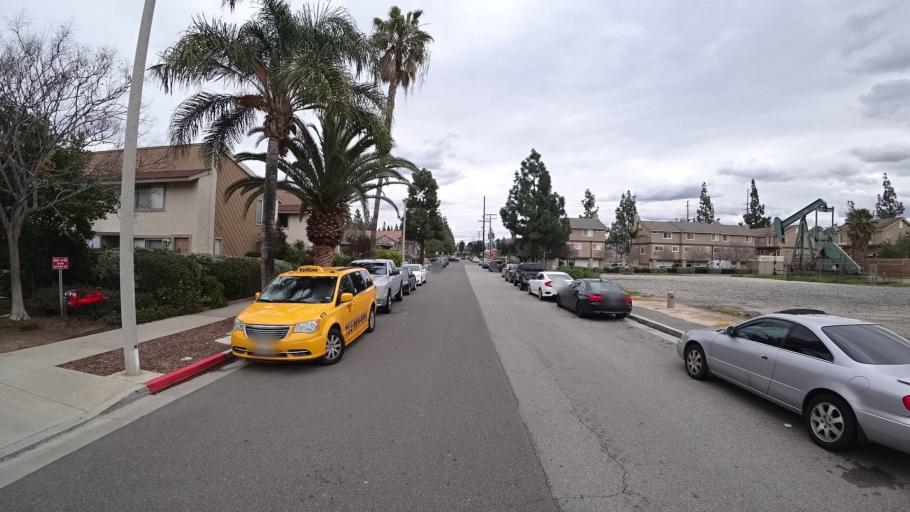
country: US
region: California
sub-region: Orange County
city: Yorba Linda
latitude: 33.8693
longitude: -117.8325
